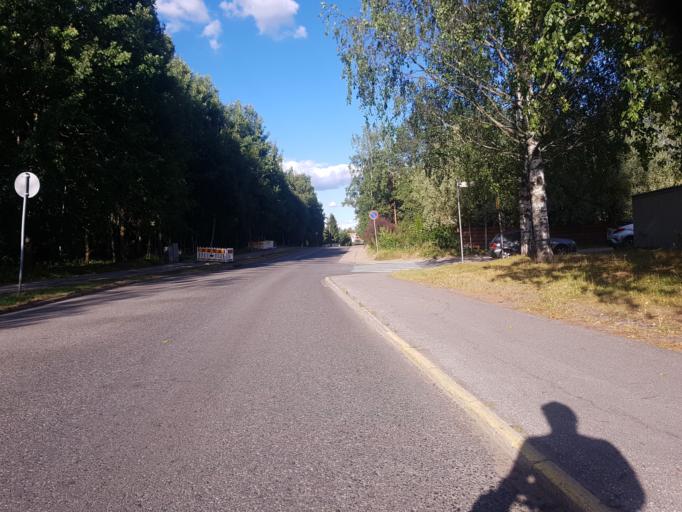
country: FI
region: Uusimaa
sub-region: Helsinki
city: Vantaa
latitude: 60.2786
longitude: 24.9953
